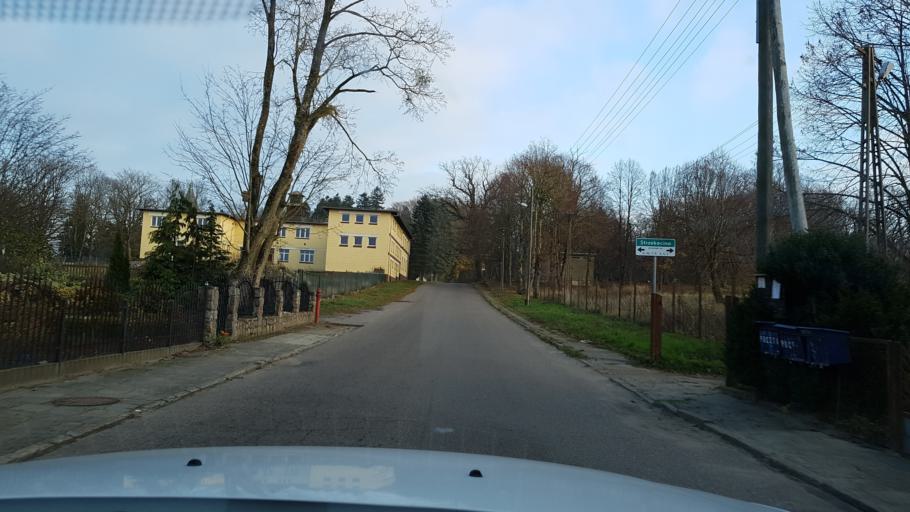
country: PL
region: West Pomeranian Voivodeship
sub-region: Koszalin
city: Koszalin
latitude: 54.1008
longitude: 16.1553
